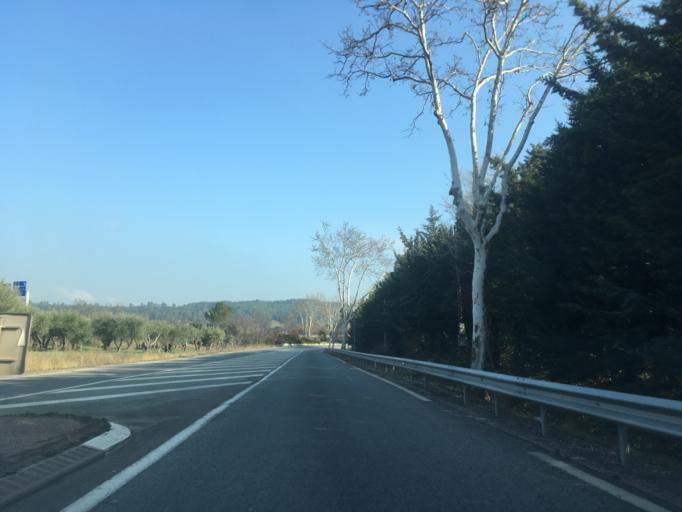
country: FR
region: Provence-Alpes-Cote d'Azur
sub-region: Departement du Var
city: Le Cannet-des-Maures
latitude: 43.3958
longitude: 6.3540
